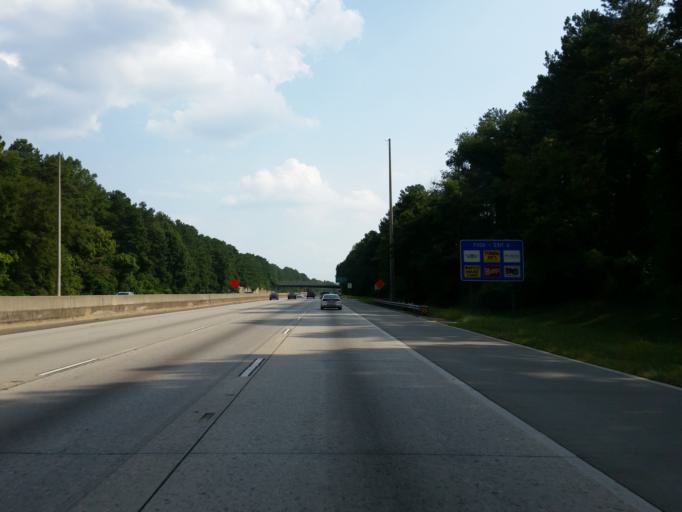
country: US
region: Georgia
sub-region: Fulton County
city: Roswell
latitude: 33.9969
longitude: -84.3374
